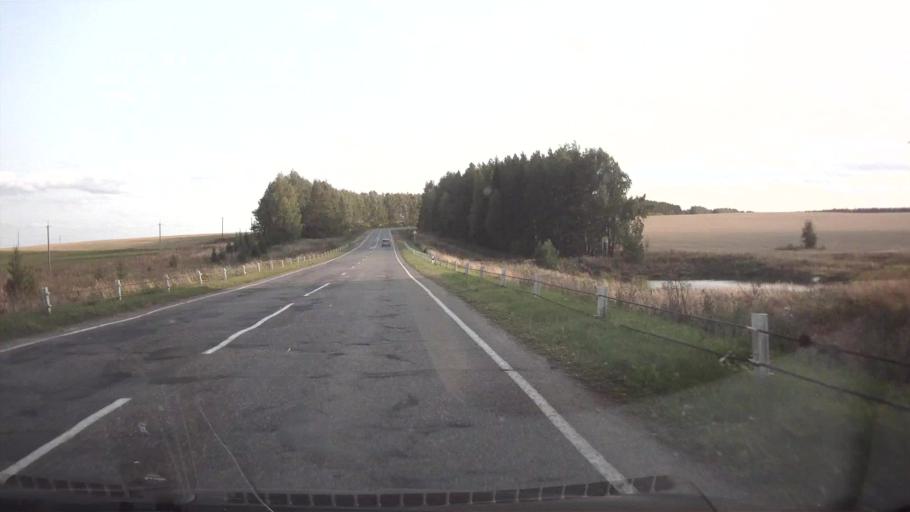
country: RU
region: Mariy-El
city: Kuzhener
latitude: 56.8628
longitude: 48.7562
